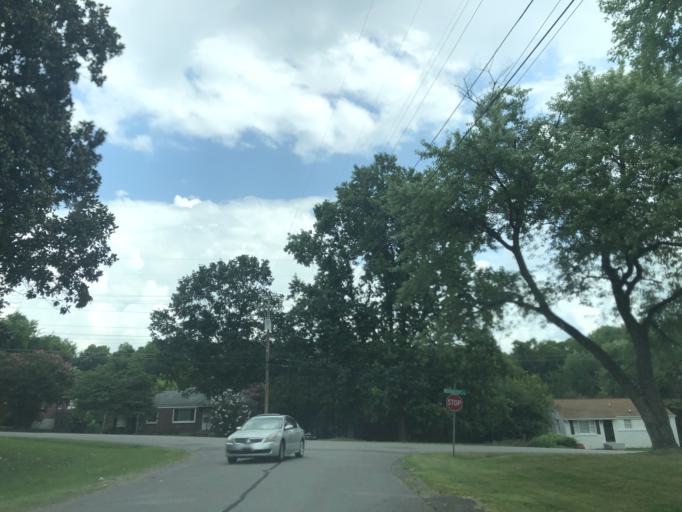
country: US
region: Tennessee
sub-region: Davidson County
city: Lakewood
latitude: 36.1600
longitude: -86.6658
